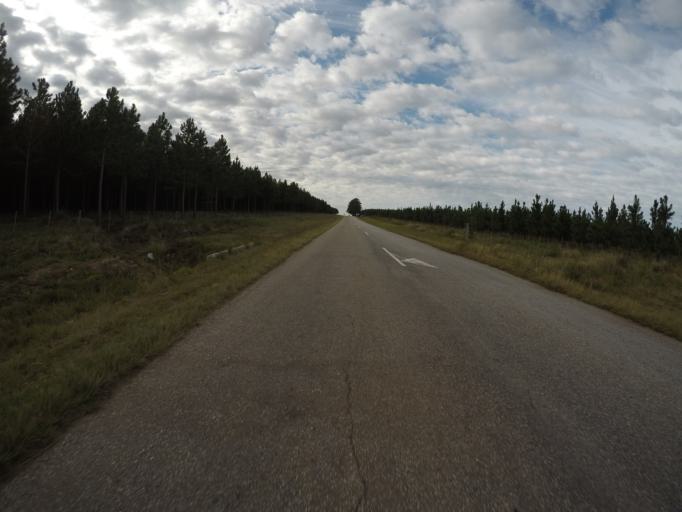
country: ZA
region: Eastern Cape
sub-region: Cacadu District Municipality
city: Kareedouw
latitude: -34.0273
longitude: 24.3724
